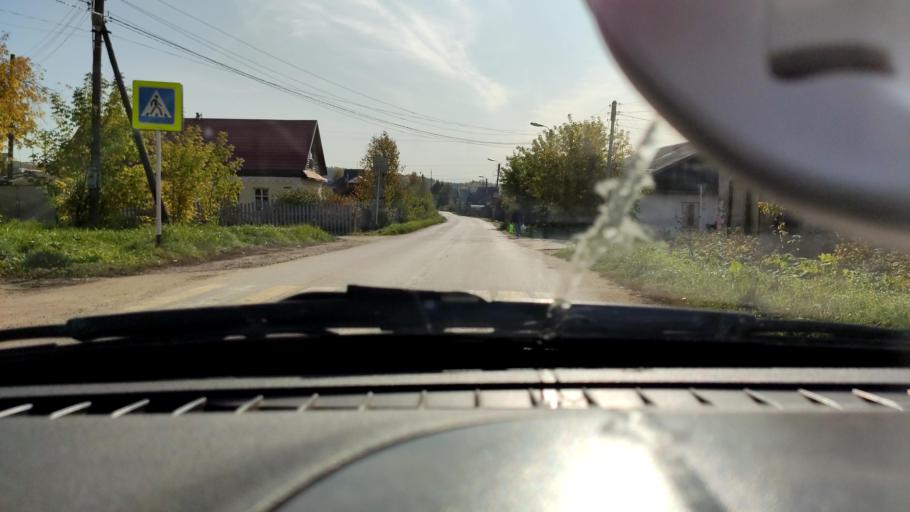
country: RU
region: Perm
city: Overyata
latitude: 58.0831
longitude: 55.8788
